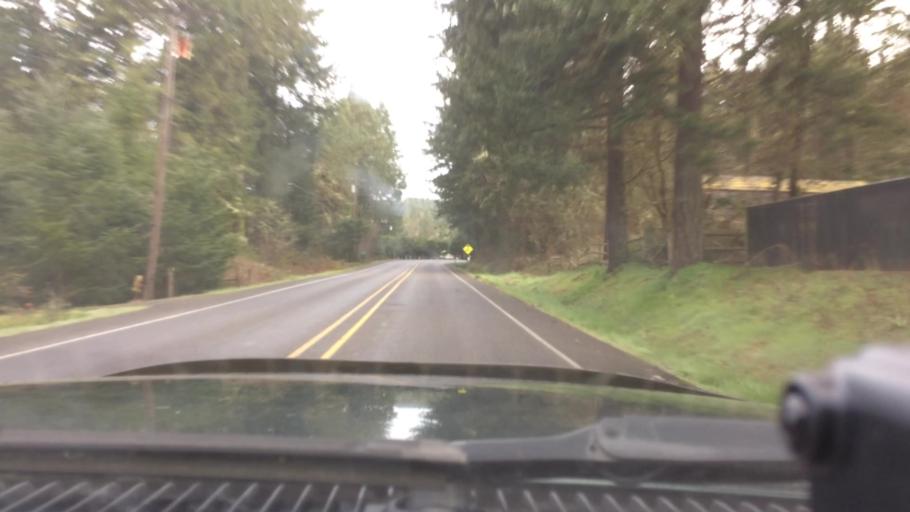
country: US
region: Oregon
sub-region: Lane County
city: Veneta
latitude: 44.1260
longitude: -123.3490
